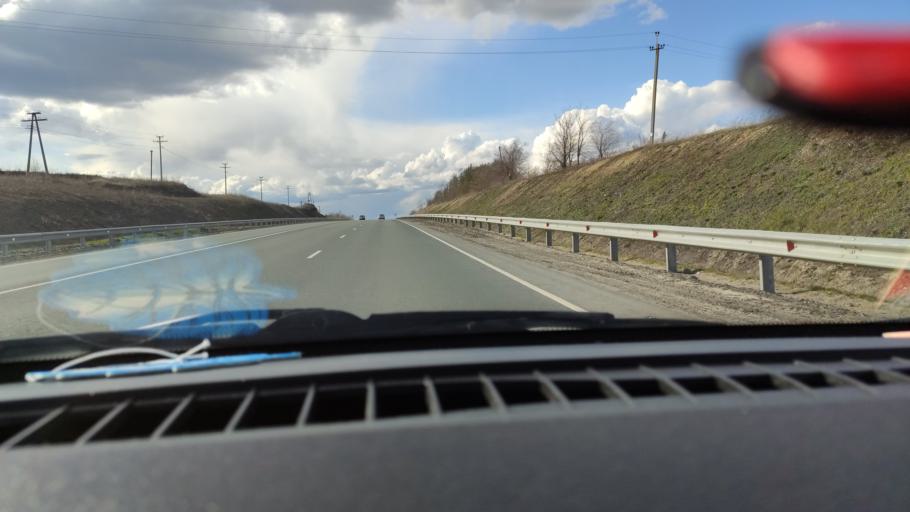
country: RU
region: Saratov
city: Shikhany
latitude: 52.1454
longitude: 47.1989
